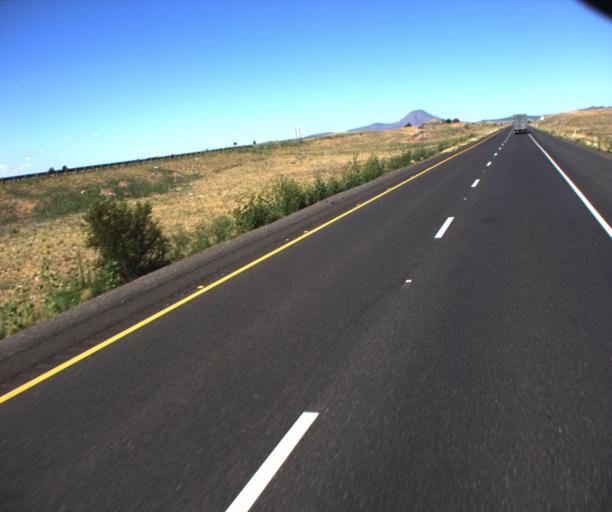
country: US
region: Arizona
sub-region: Yavapai County
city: Paulden
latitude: 35.2311
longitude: -112.5953
